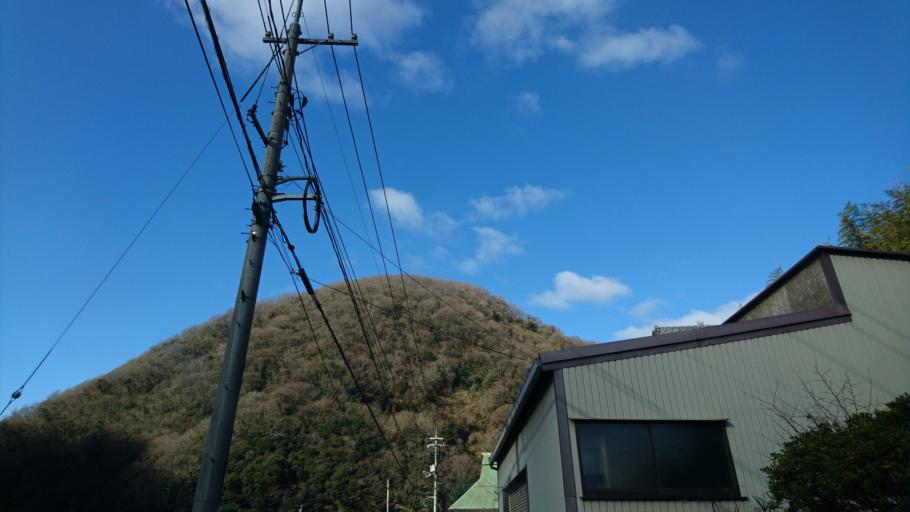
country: JP
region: Okayama
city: Takahashi
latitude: 34.8556
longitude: 133.5719
